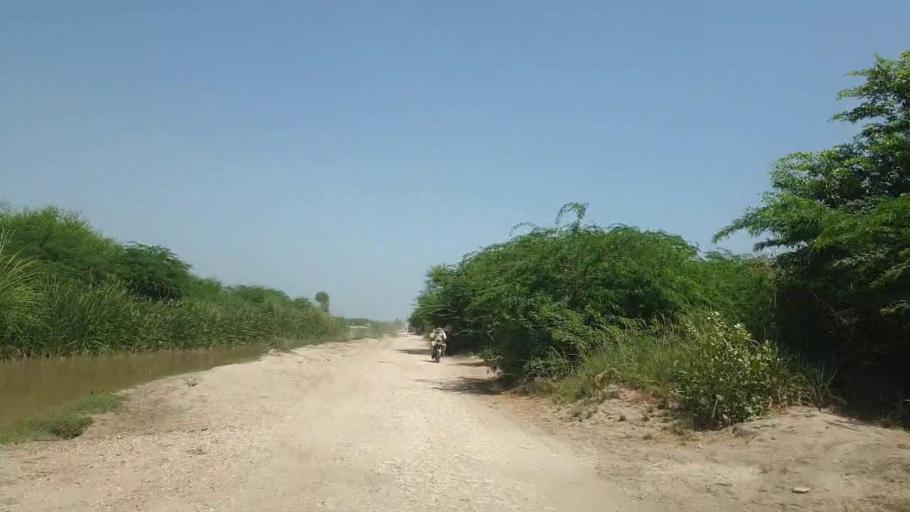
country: PK
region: Sindh
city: Rohri
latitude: 27.6328
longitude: 69.1000
